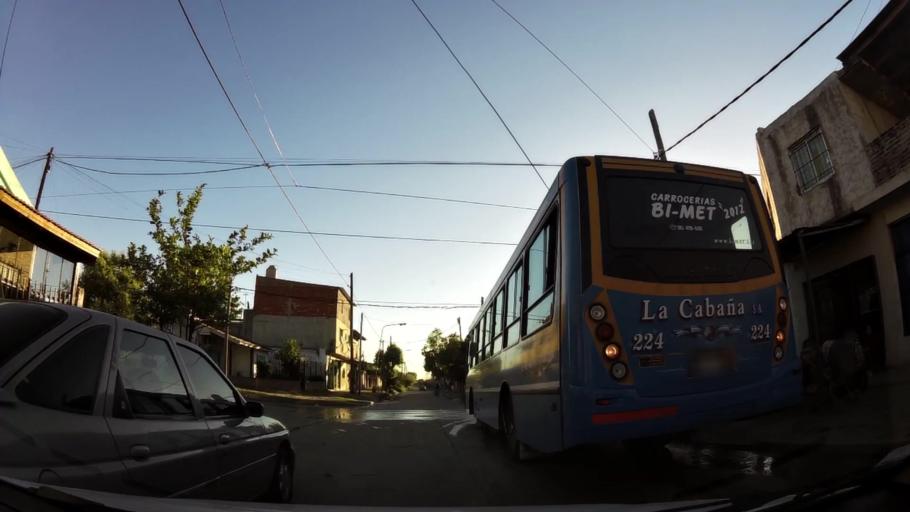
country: AR
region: Buenos Aires
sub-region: Partido de Moron
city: Moron
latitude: -34.7157
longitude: -58.6151
